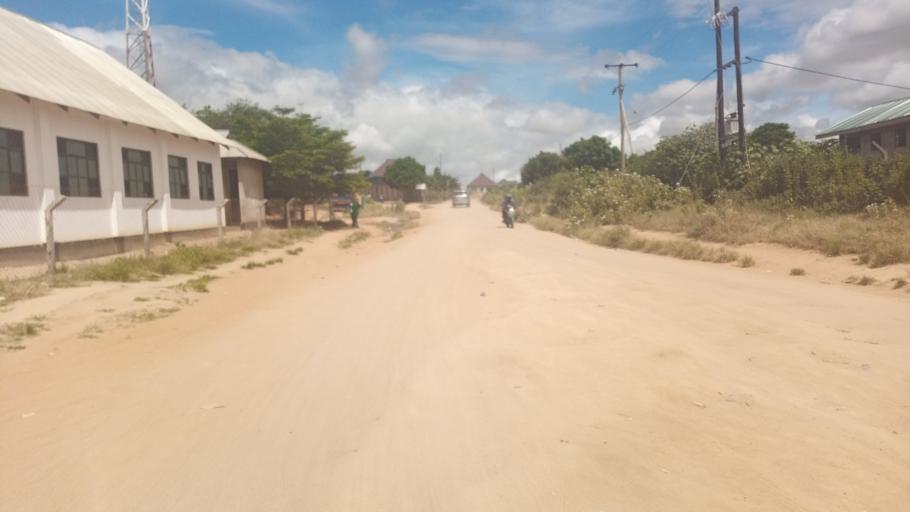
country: TZ
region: Dodoma
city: Dodoma
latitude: -6.1854
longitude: 35.7313
